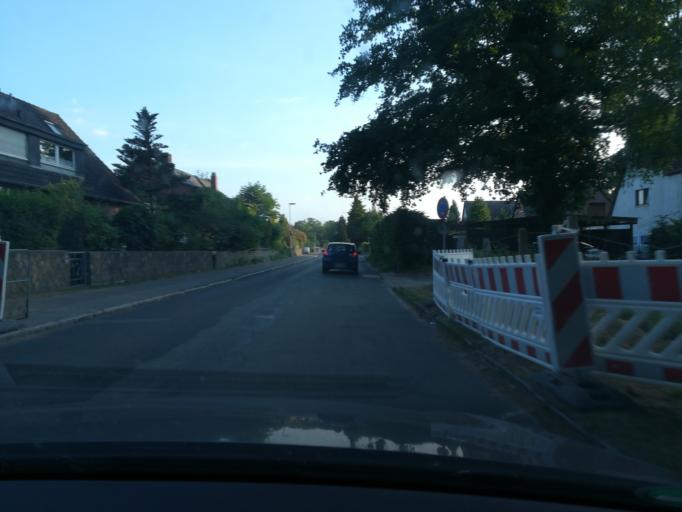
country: DE
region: Schleswig-Holstein
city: Grossensee
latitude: 53.6119
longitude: 10.3418
